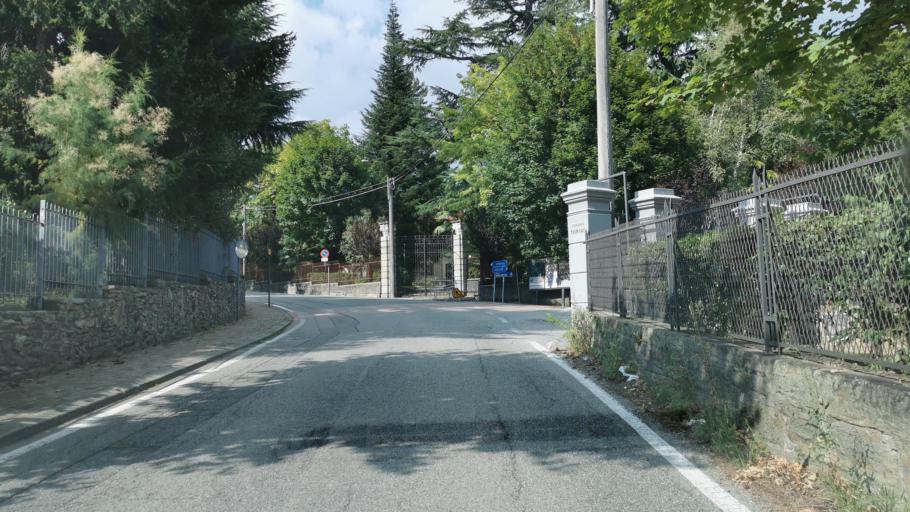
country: IT
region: Piedmont
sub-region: Provincia di Torino
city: Corio
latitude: 45.3096
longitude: 7.5362
